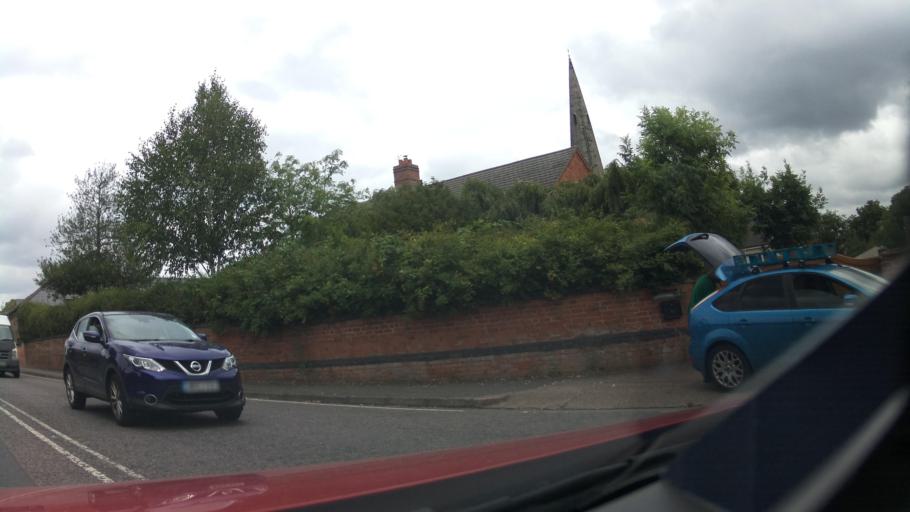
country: GB
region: England
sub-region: Derbyshire
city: Long Eaton
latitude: 52.8770
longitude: -1.3007
